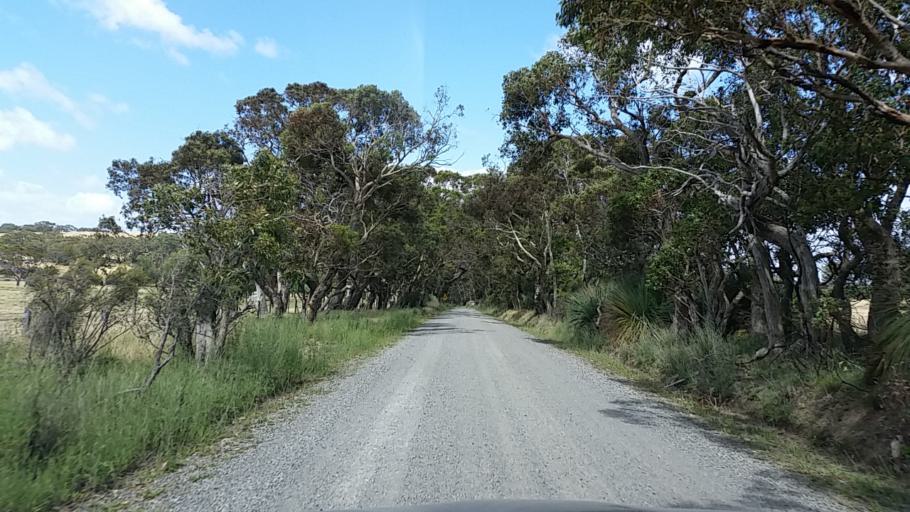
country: AU
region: South Australia
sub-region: Alexandrina
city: Mount Compass
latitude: -35.4362
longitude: 138.5887
